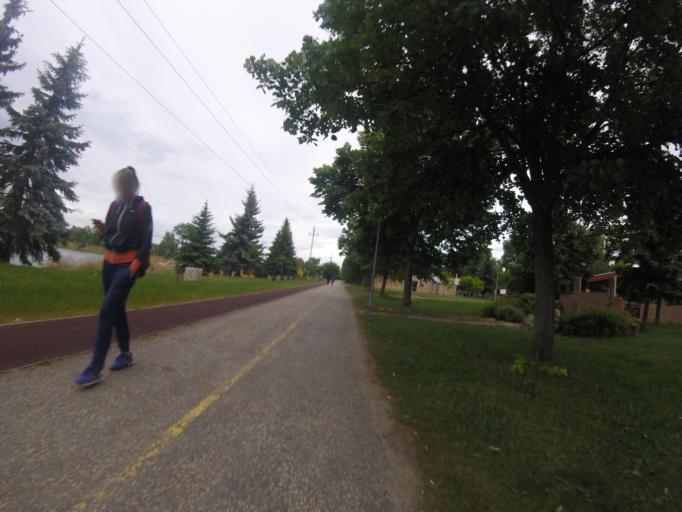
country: HU
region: Pest
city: Budakalasz
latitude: 47.6157
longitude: 19.0629
